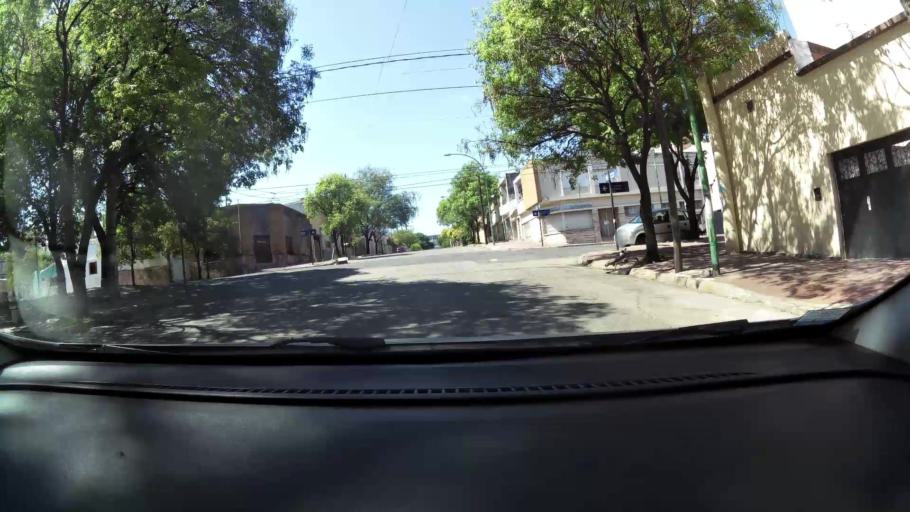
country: AR
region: Cordoba
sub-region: Departamento de Capital
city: Cordoba
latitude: -31.4036
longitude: -64.1771
